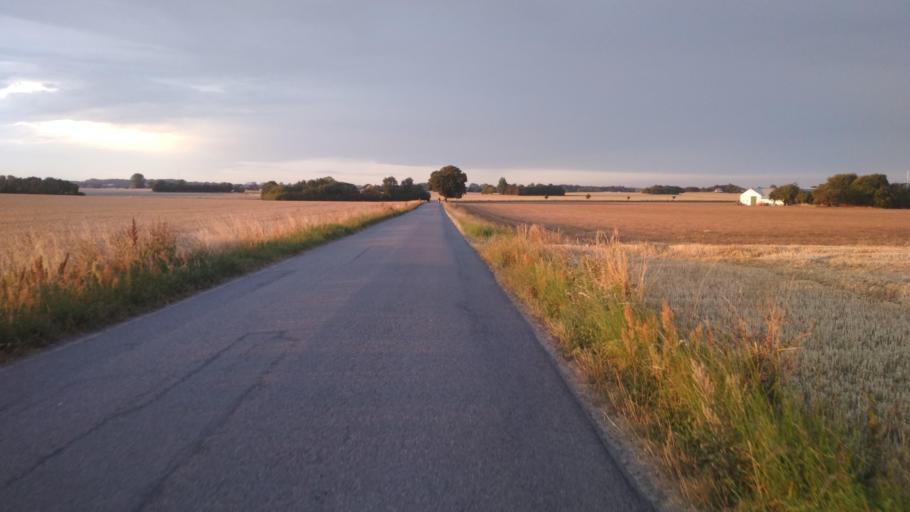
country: DK
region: Capital Region
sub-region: Bornholm Kommune
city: Akirkeby
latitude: 55.0307
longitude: 14.9128
